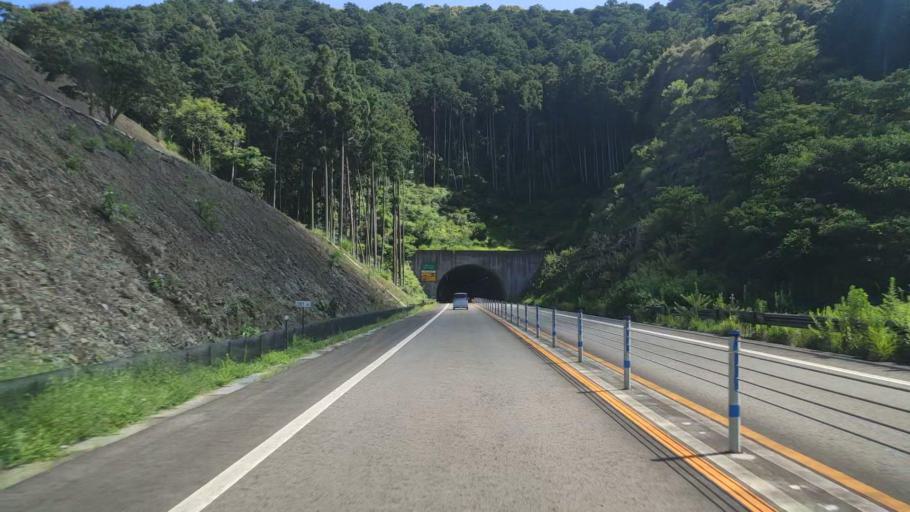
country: JP
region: Wakayama
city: Shingu
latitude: 33.6180
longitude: 135.9175
